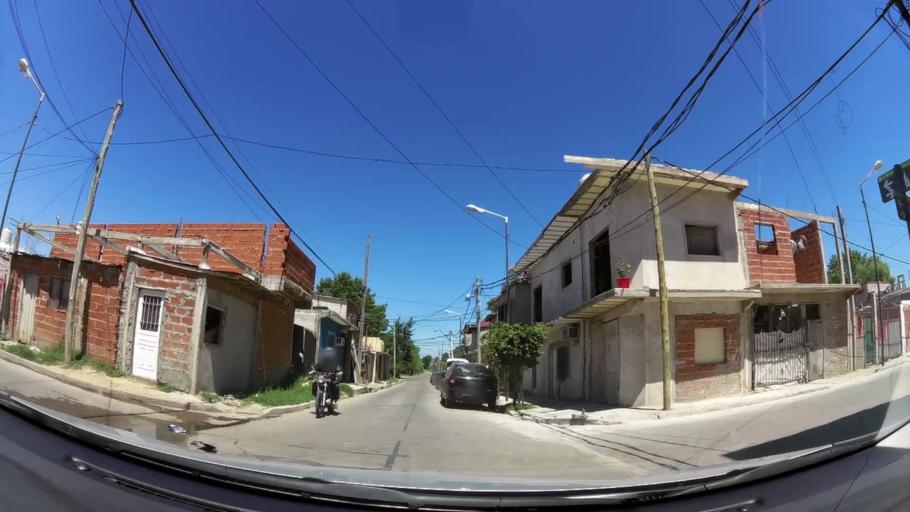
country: AR
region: Buenos Aires
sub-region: Partido de Tigre
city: Tigre
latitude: -34.4602
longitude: -58.5525
